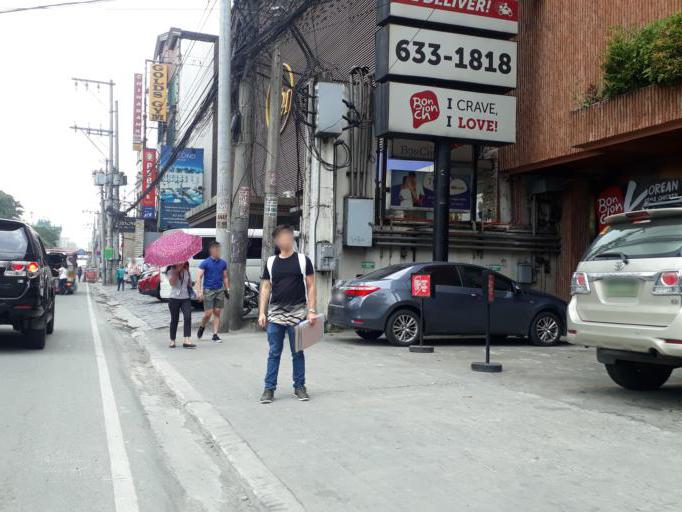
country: PH
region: Metro Manila
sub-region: Marikina
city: Calumpang
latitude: 14.6054
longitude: 121.0790
